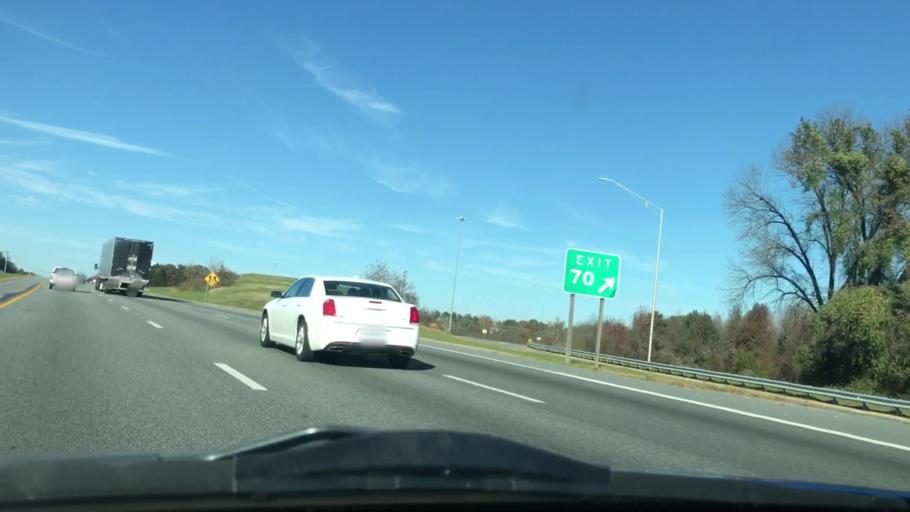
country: US
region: North Carolina
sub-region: Guilford County
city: High Point
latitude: 35.9627
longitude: -79.9745
